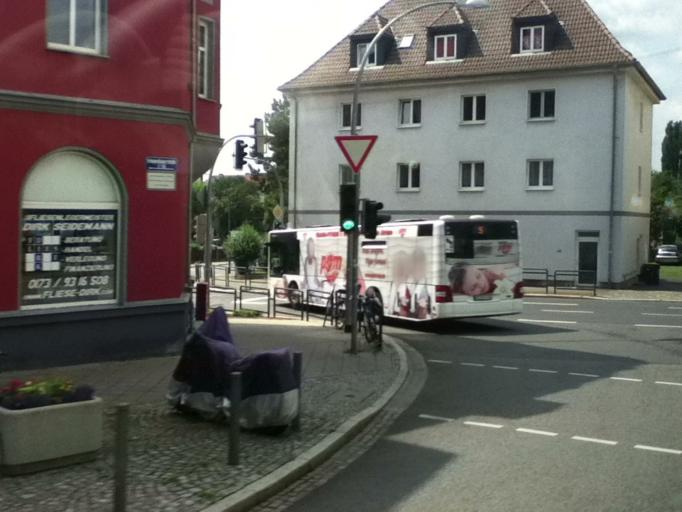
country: DE
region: Thuringia
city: Weimar
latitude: 50.9911
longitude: 11.3220
